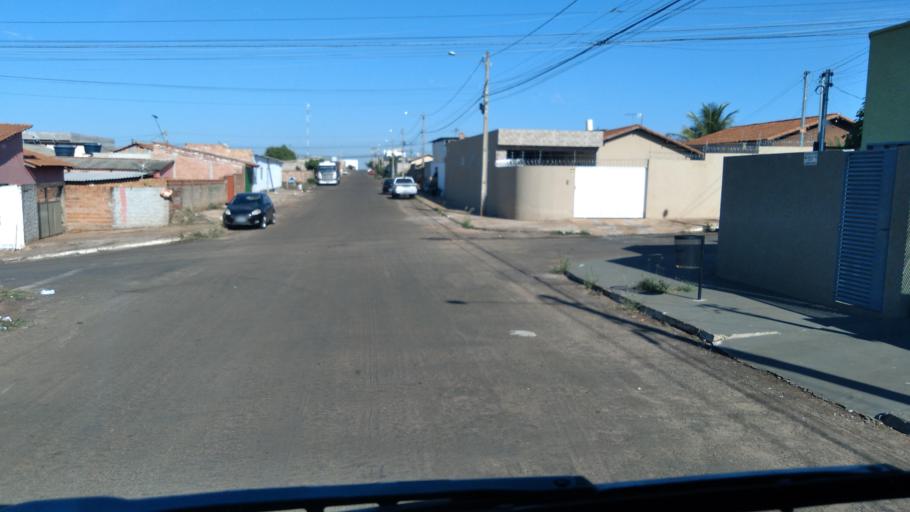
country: BR
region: Goias
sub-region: Mineiros
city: Mineiros
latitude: -17.5735
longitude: -52.5723
